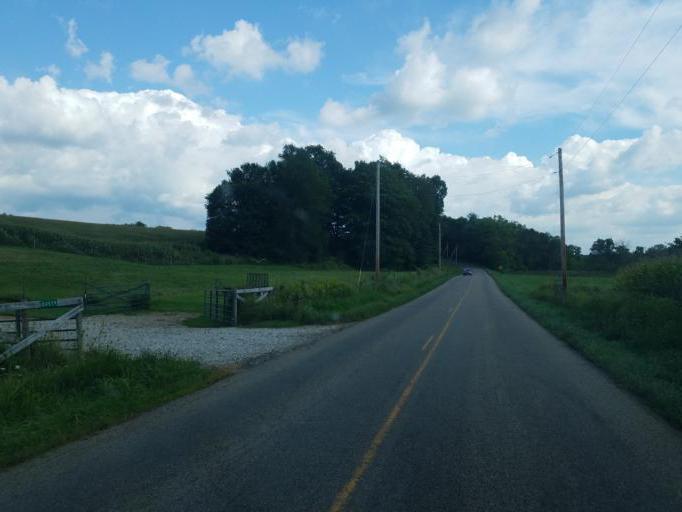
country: US
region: Ohio
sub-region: Knox County
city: Danville
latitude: 40.4615
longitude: -82.3027
